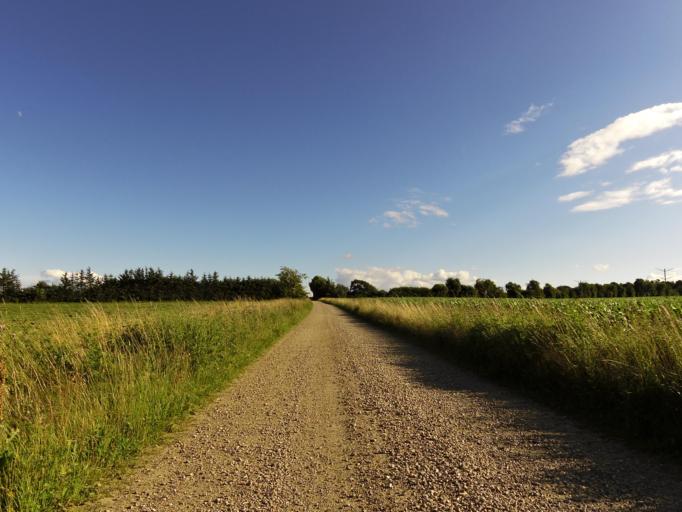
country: DK
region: South Denmark
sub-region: Vejen Kommune
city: Rodding
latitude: 55.3144
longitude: 9.1702
